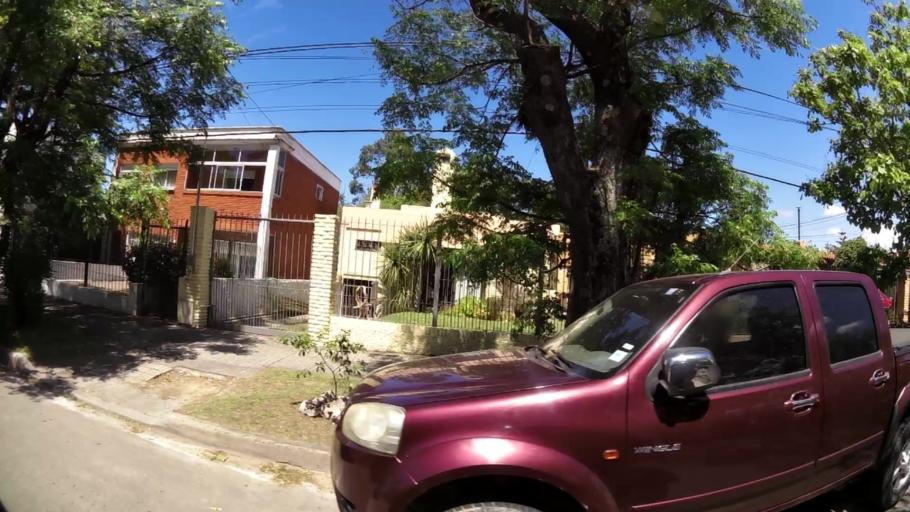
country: UY
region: Canelones
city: Paso de Carrasco
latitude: -34.8886
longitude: -56.0968
